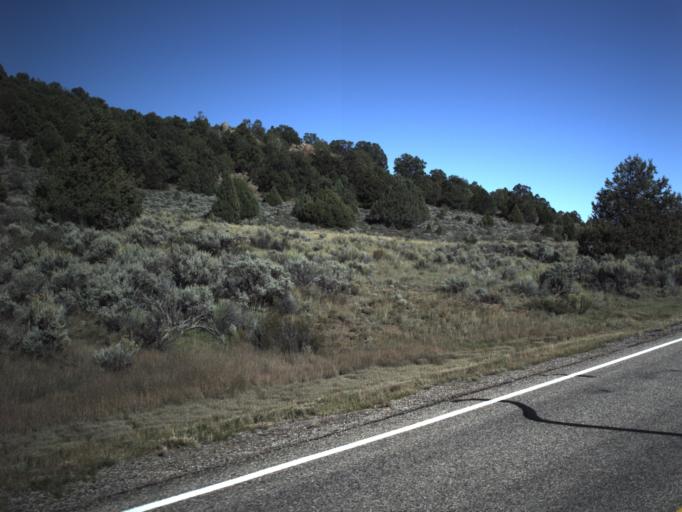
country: US
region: Utah
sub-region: Garfield County
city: Panguitch
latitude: 37.7632
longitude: -112.5286
